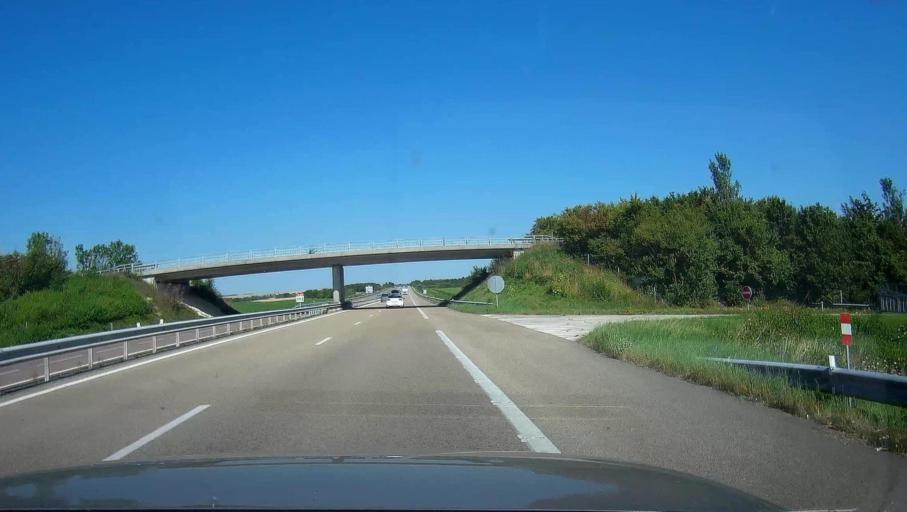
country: FR
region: Champagne-Ardenne
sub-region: Departement de l'Aube
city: Creney-pres-Troyes
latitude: 48.3371
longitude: 4.1670
